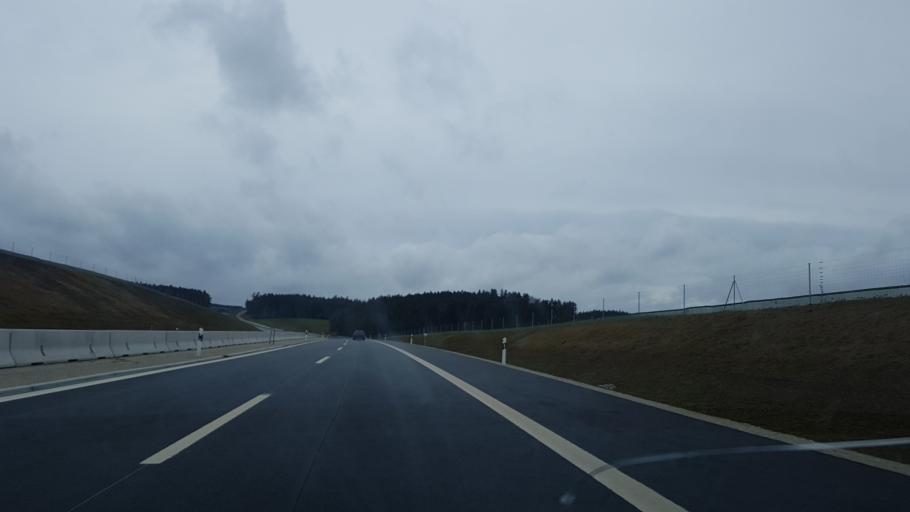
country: DE
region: Bavaria
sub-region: Lower Bavaria
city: Essenbach
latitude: 48.6423
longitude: 12.2013
